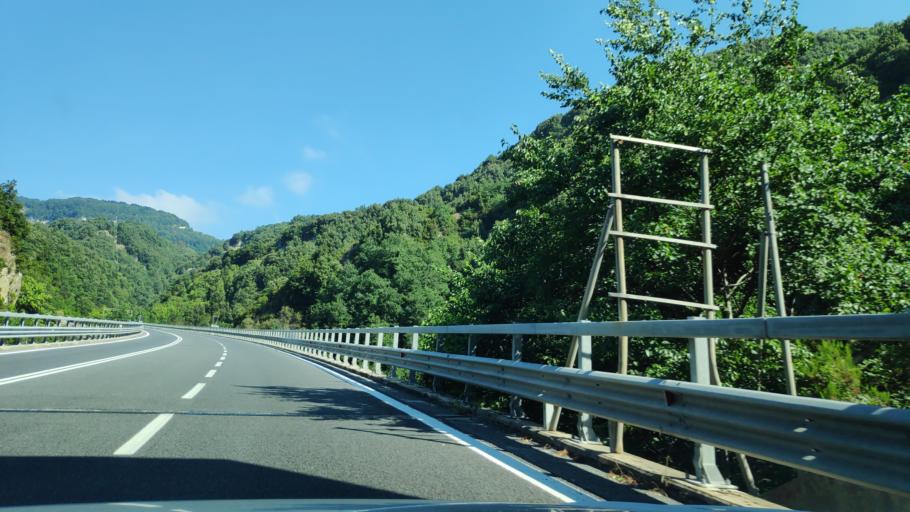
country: IT
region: Calabria
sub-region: Provincia di Reggio Calabria
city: Amato
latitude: 38.3709
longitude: 16.1820
